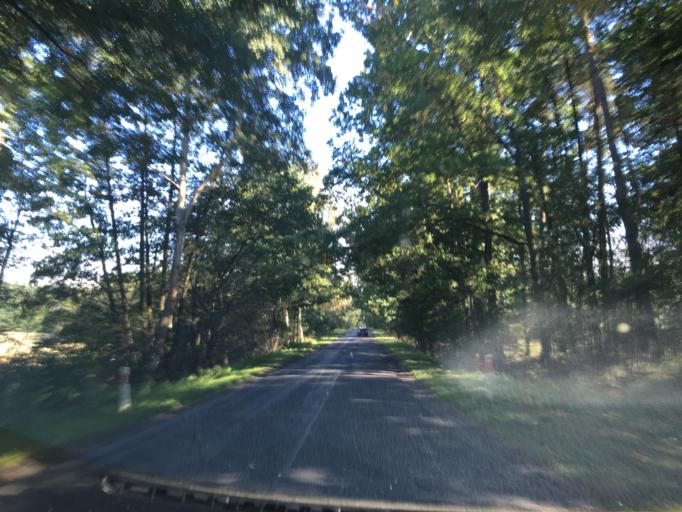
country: PL
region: Kujawsko-Pomorskie
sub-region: Powiat swiecki
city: Warlubie
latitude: 53.5982
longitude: 18.5758
